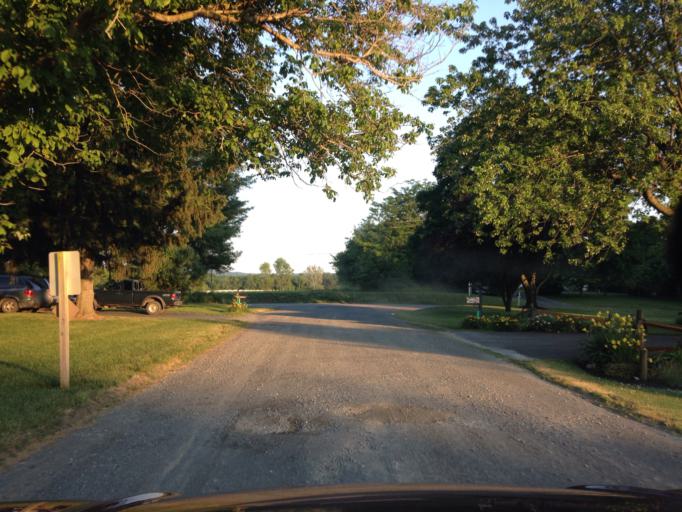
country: US
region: Virginia
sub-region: Loudoun County
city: Lovettsville
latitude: 39.2680
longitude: -77.6233
